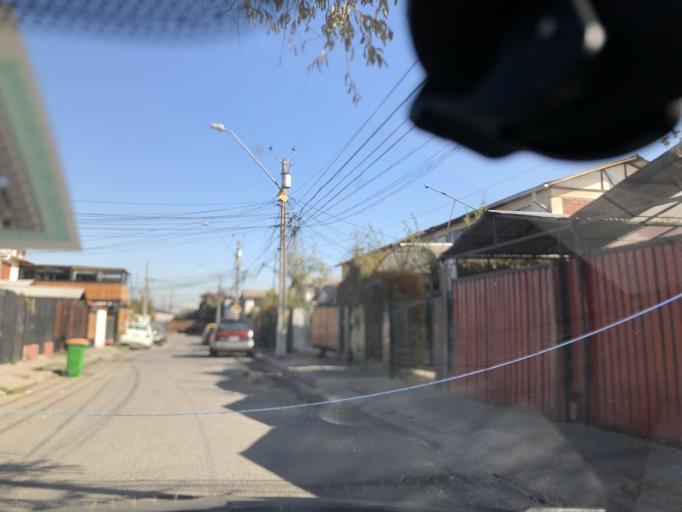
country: CL
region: Santiago Metropolitan
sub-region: Provincia de Cordillera
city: Puente Alto
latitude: -33.5839
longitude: -70.5897
